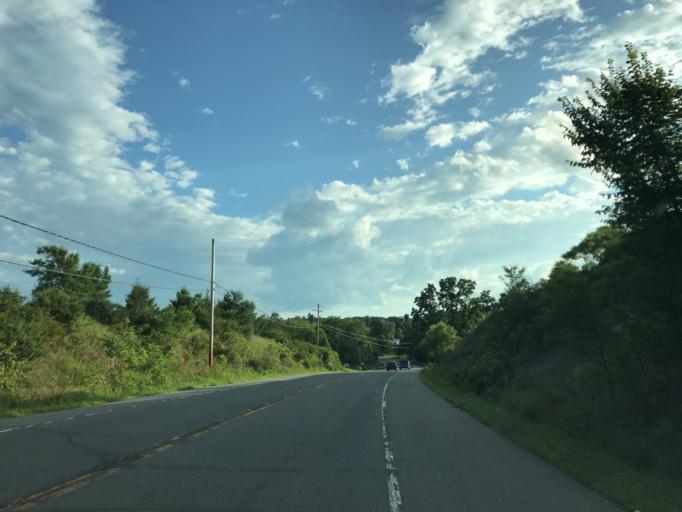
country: US
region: New York
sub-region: Saratoga County
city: Schuylerville
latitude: 43.0634
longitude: -73.5904
